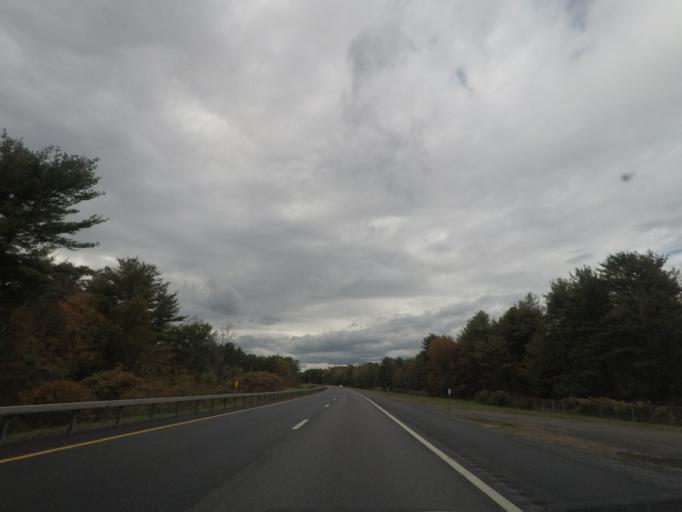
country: US
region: New York
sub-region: Rensselaer County
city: Castleton-on-Hudson
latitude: 42.4940
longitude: -73.7118
